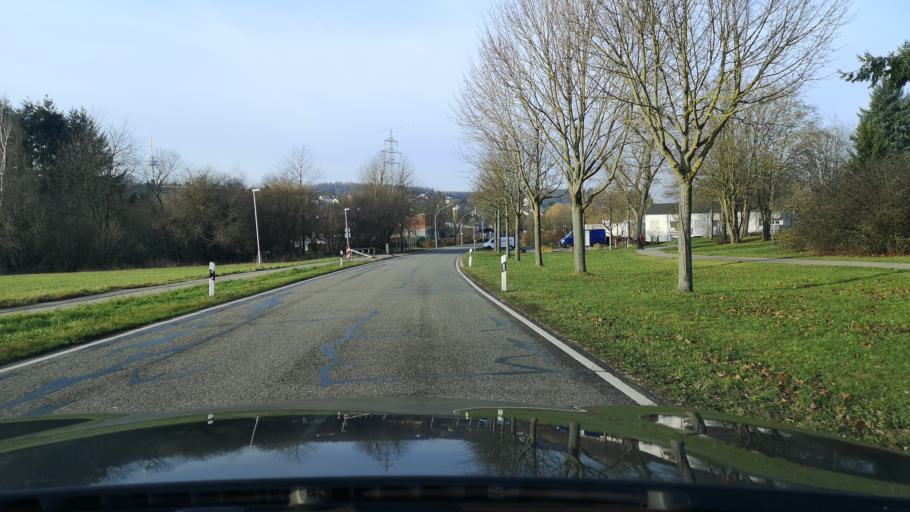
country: DE
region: Baden-Wuerttemberg
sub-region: Karlsruhe Region
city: Ettlingen
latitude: 48.9496
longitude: 8.4737
